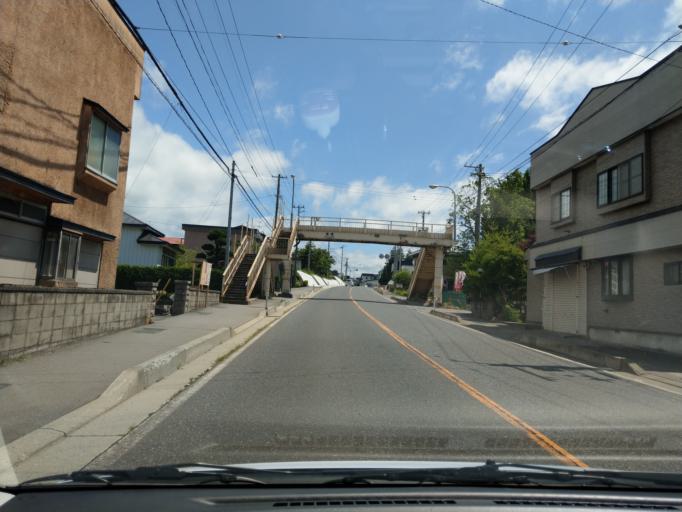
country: JP
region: Aomori
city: Kuroishi
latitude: 40.5144
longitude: 140.6032
